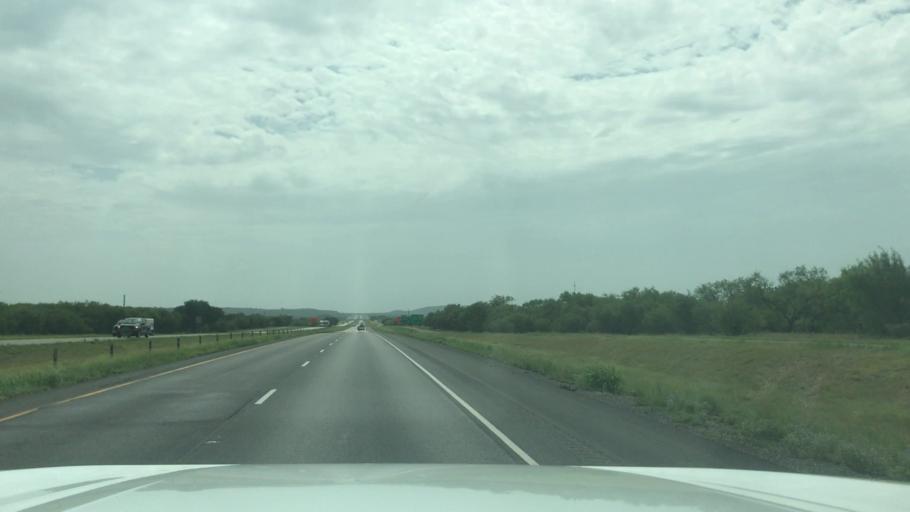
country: US
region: Texas
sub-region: Callahan County
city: Baird
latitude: 32.3801
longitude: -99.2665
